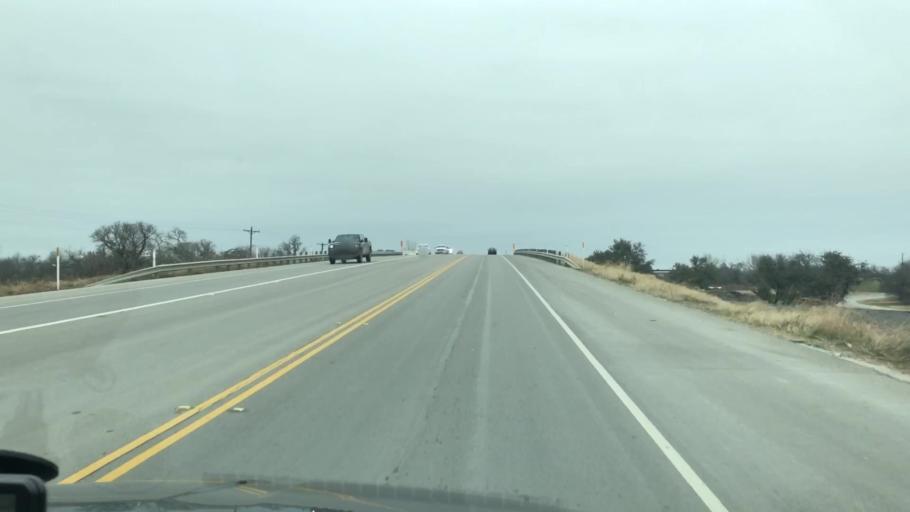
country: US
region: Texas
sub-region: Erath County
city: Stephenville
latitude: 32.2379
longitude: -98.1942
